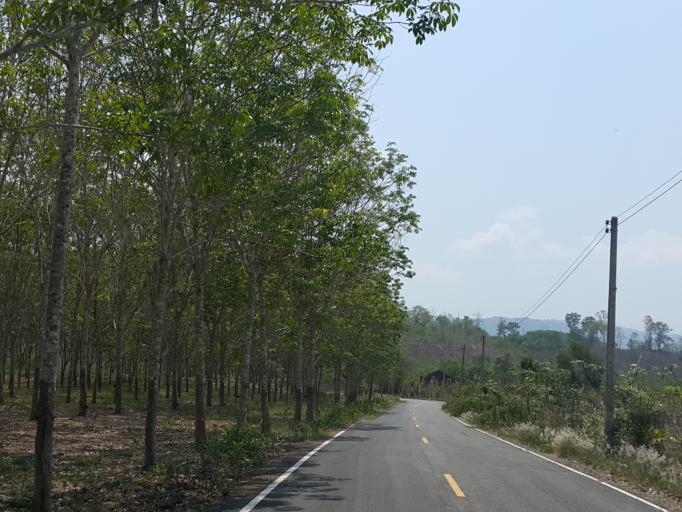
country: TH
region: Kanchanaburi
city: Sai Yok
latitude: 14.1831
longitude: 98.9565
